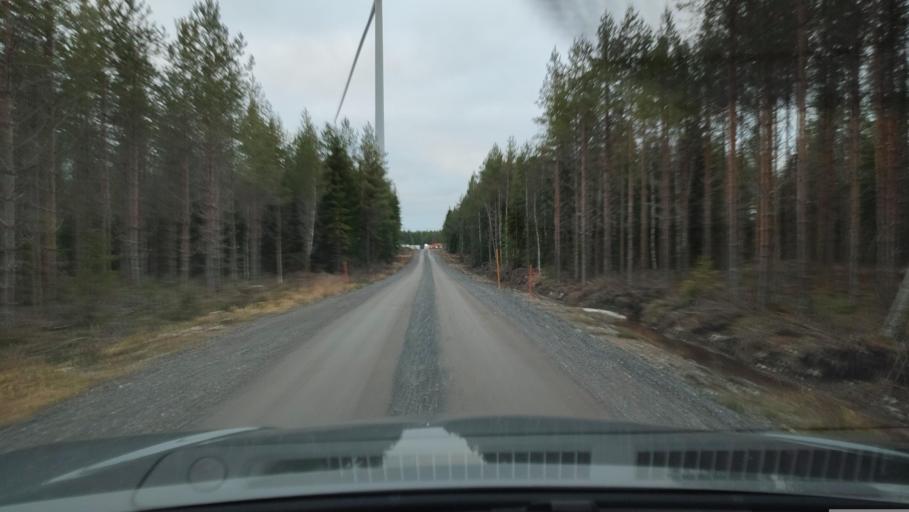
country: FI
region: Southern Ostrobothnia
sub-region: Suupohja
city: Karijoki
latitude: 62.1850
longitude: 21.5624
